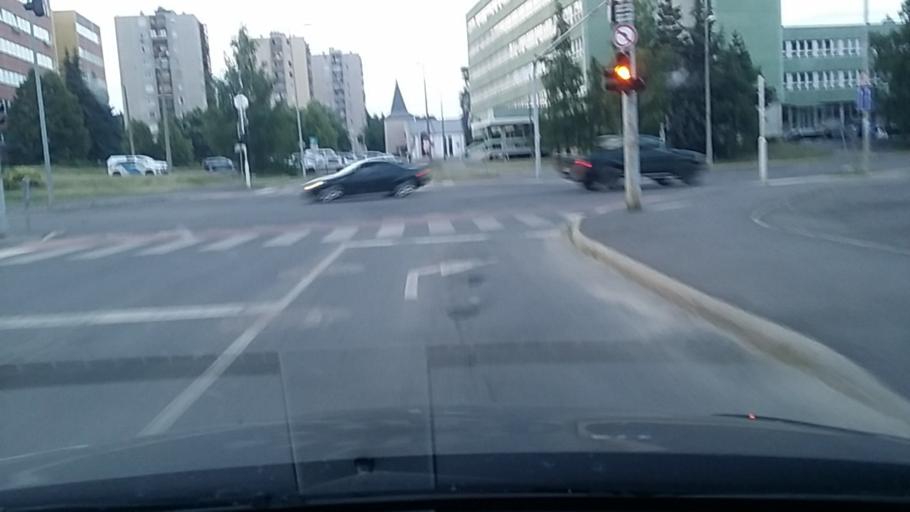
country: HU
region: Borsod-Abauj-Zemplen
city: Miskolc
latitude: 48.1064
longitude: 20.7762
